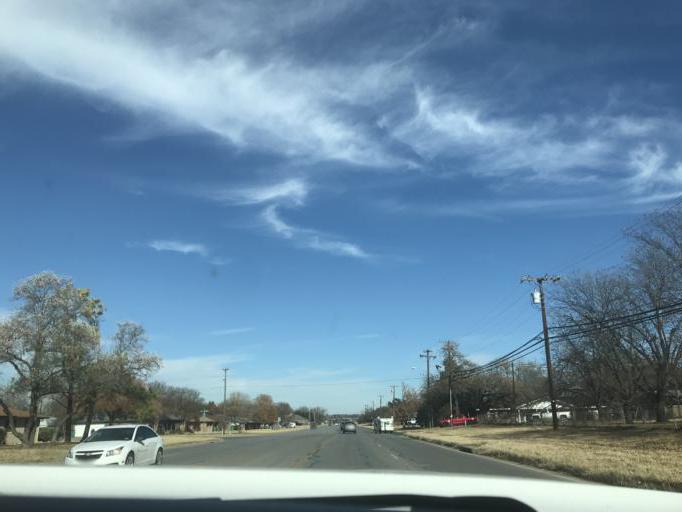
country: US
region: Texas
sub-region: Erath County
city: Stephenville
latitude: 32.2268
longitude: -98.2206
